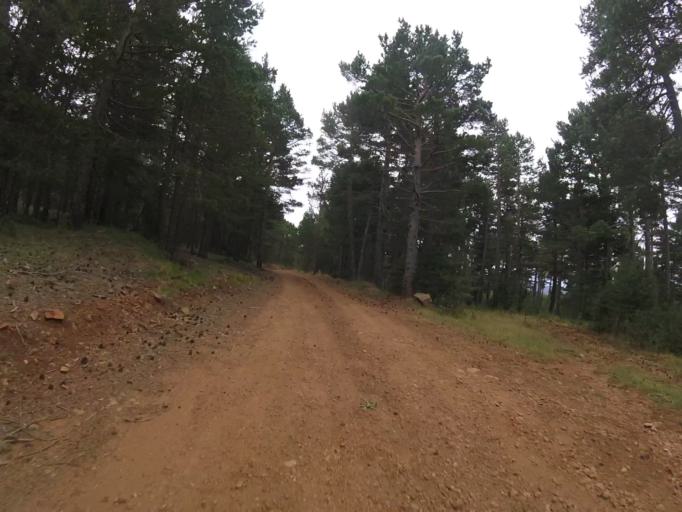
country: ES
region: Aragon
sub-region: Provincia de Teruel
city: Valdelinares
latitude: 40.3697
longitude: -0.6201
